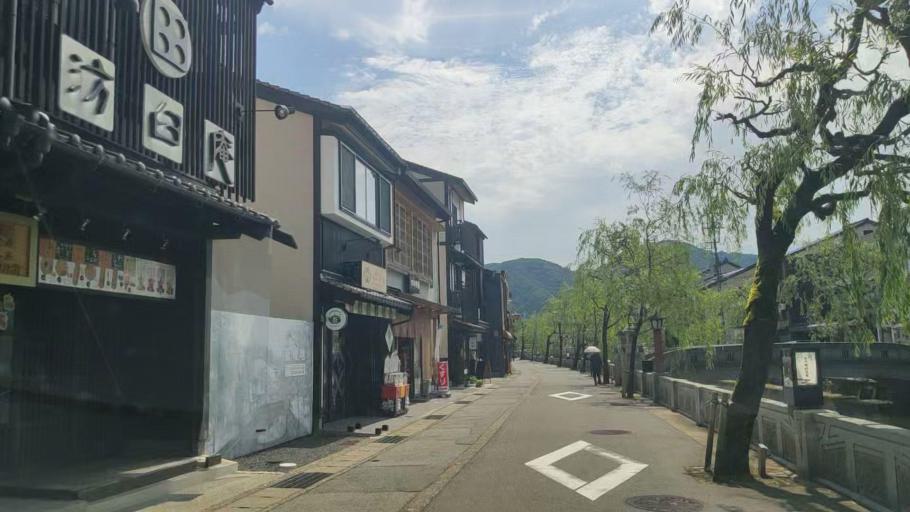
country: JP
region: Hyogo
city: Toyooka
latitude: 35.6269
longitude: 134.8099
